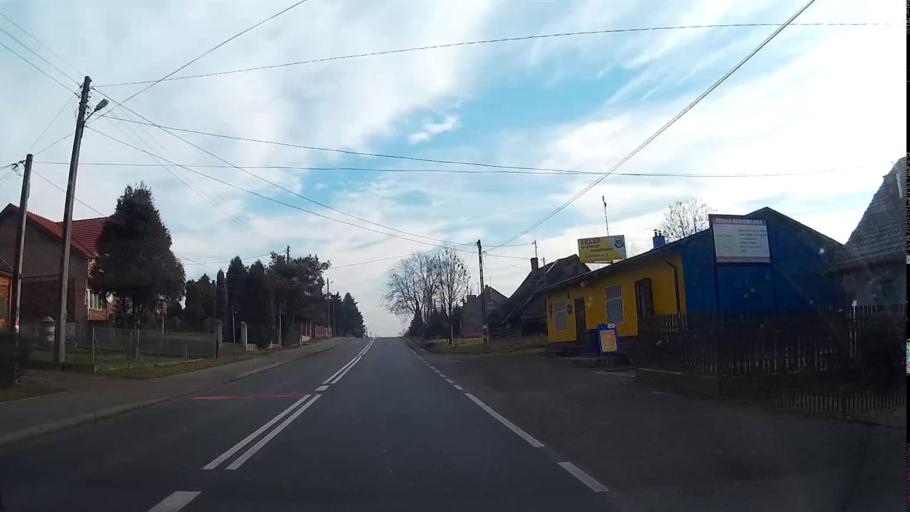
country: PL
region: Lesser Poland Voivodeship
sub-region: Powiat krakowski
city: Kaszow
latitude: 50.0393
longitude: 19.7263
